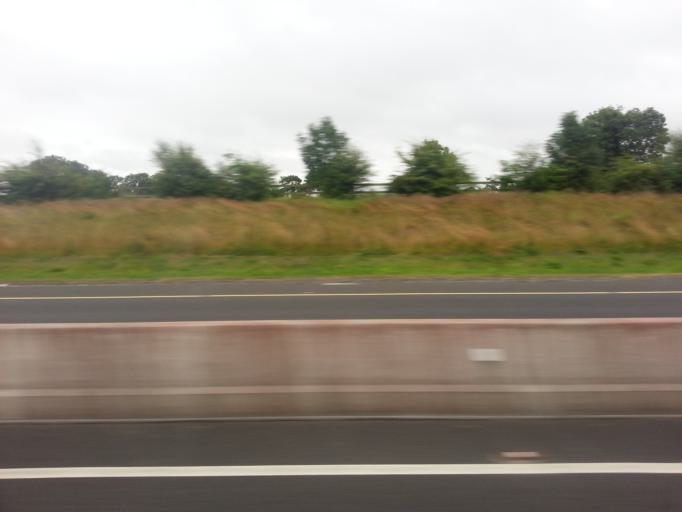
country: IE
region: Leinster
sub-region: County Carlow
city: Bagenalstown
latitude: 52.7645
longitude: -6.9685
